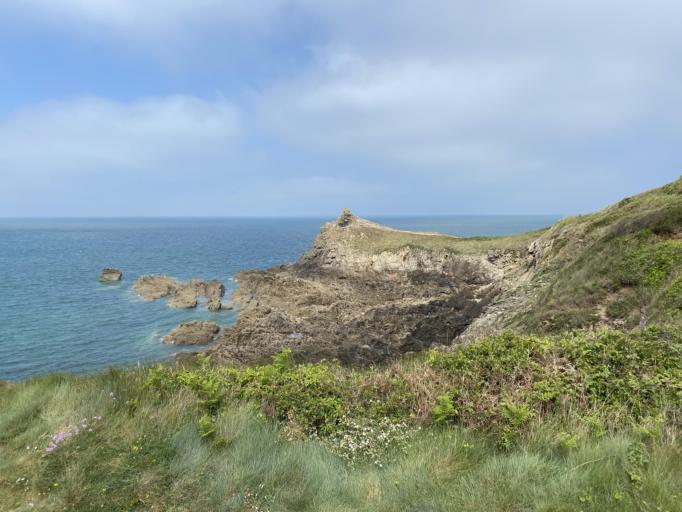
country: FR
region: Brittany
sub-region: Departement d'Ille-et-Vilaine
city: Cancale
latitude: 48.6998
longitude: -1.8690
